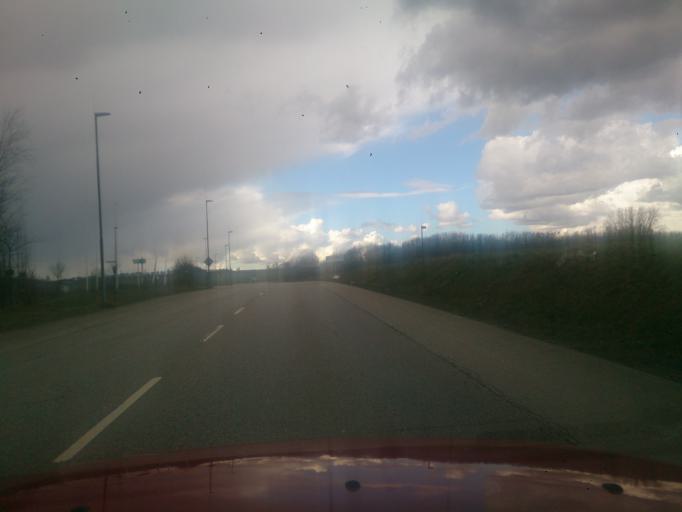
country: SE
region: Skane
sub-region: Ystads Kommun
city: Ystad
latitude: 55.4306
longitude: 13.7773
